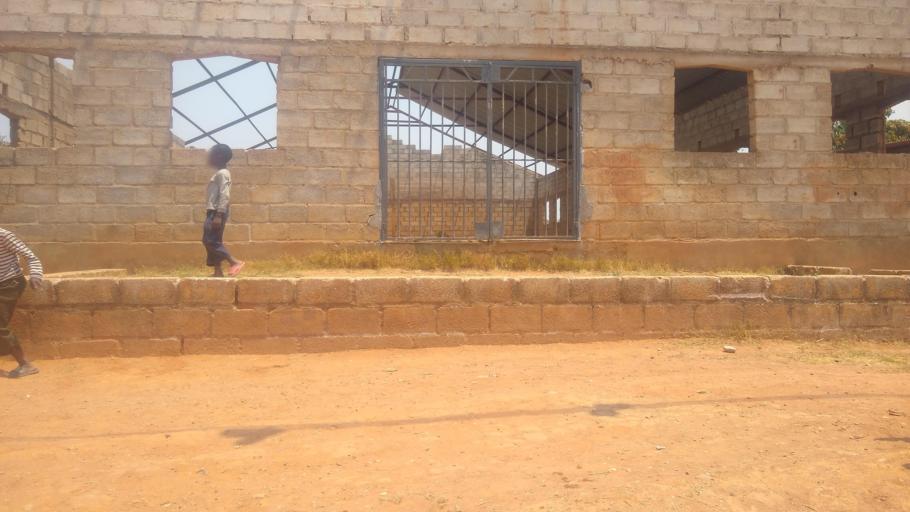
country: ZM
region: Lusaka
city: Lusaka
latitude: -15.4356
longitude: 28.3772
